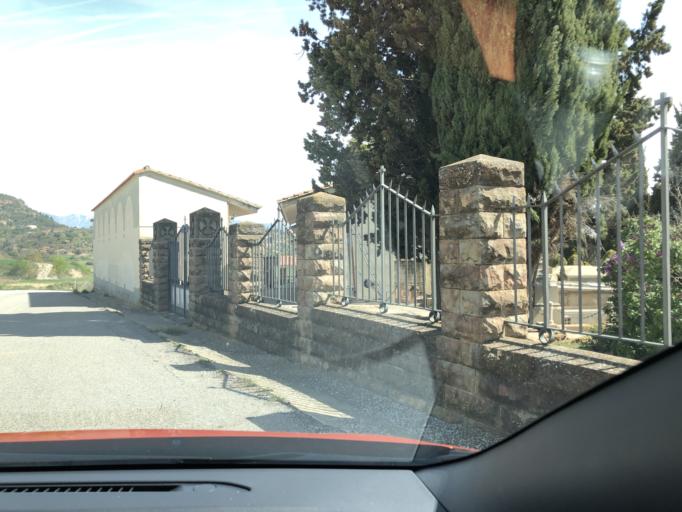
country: ES
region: Catalonia
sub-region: Provincia de Lleida
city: Solsona
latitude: 41.9996
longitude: 1.5241
